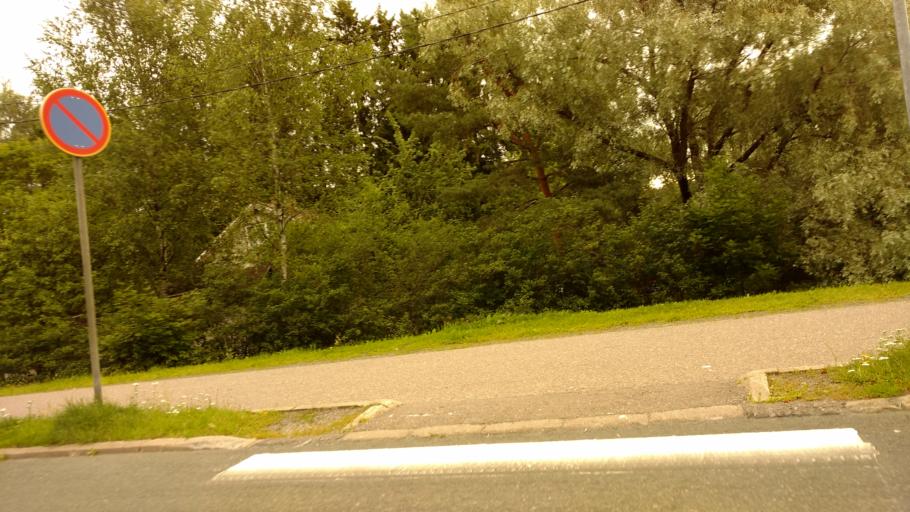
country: FI
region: Varsinais-Suomi
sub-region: Turku
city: Kaarina
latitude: 60.4396
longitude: 22.3554
